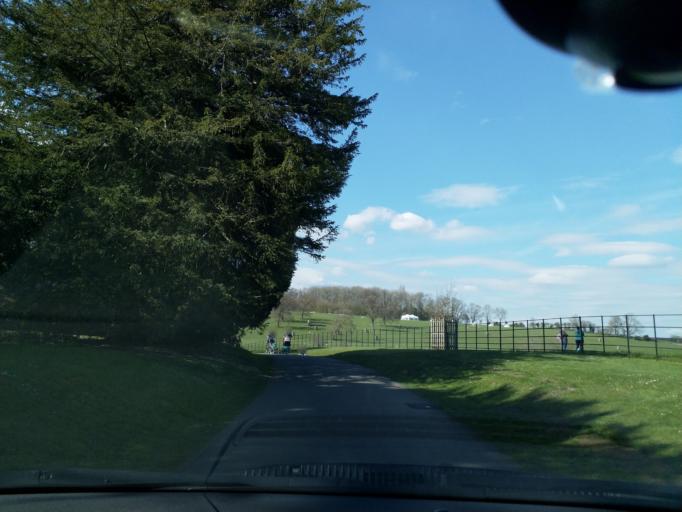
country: GB
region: England
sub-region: Warwickshire
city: Wellesbourne Mountford
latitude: 52.1726
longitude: -1.5430
